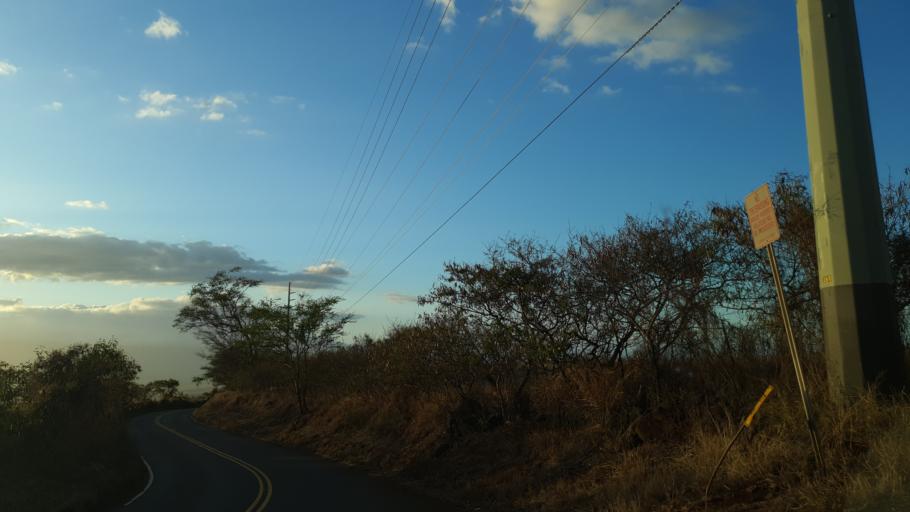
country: US
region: Hawaii
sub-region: Maui County
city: Pukalani
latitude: 20.7875
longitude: -156.3512
